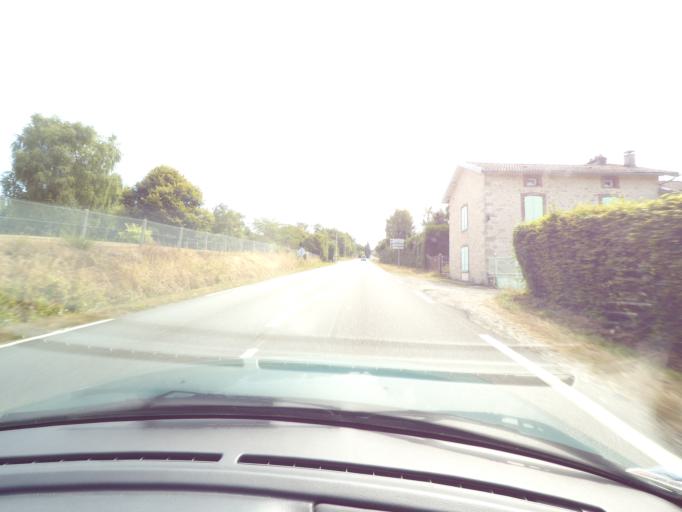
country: FR
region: Limousin
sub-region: Departement de la Haute-Vienne
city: Feytiat
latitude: 45.8009
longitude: 1.3826
